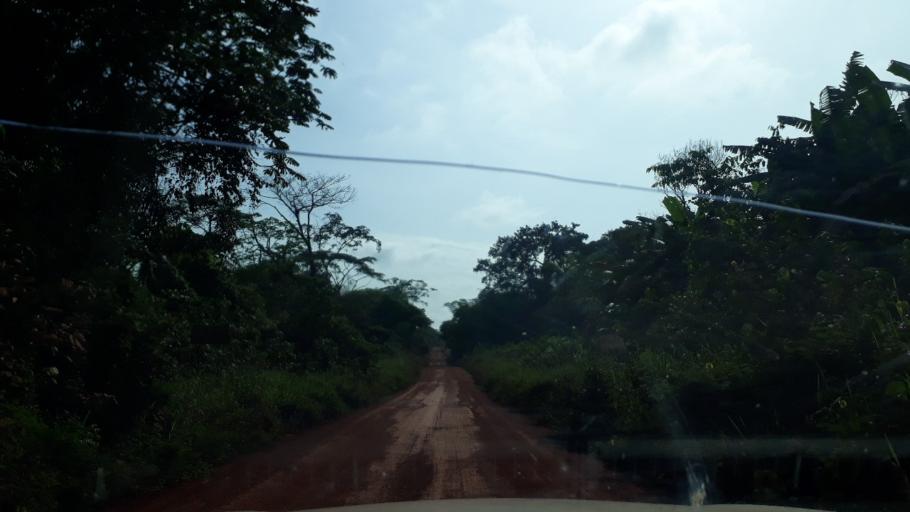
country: CD
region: Eastern Province
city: Wamba
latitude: 1.3997
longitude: 27.6783
